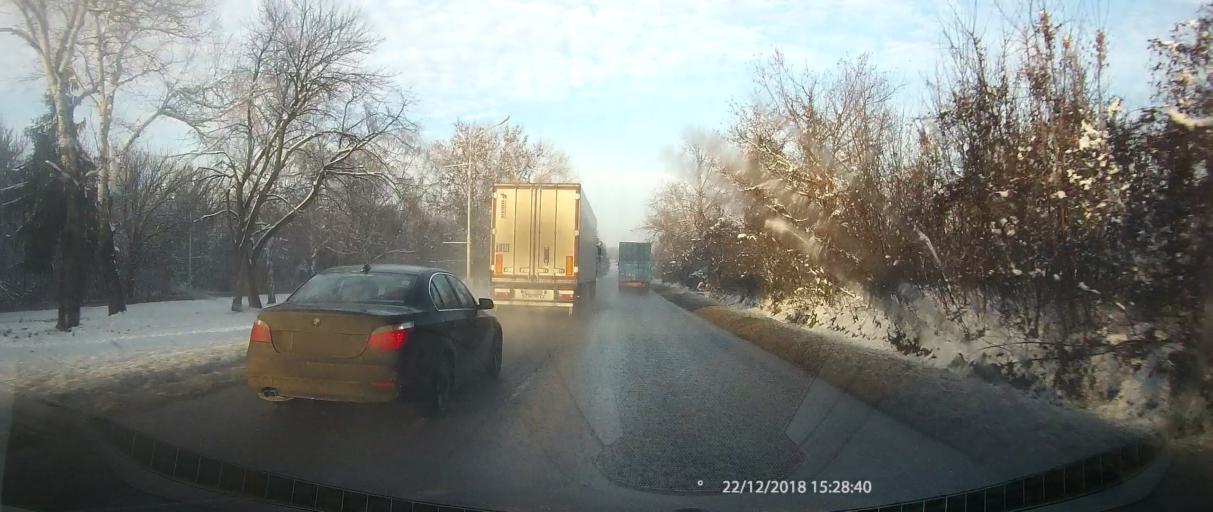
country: RO
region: Giurgiu
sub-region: Comuna Slobozia
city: Slobozia
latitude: 43.8012
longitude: 25.9202
